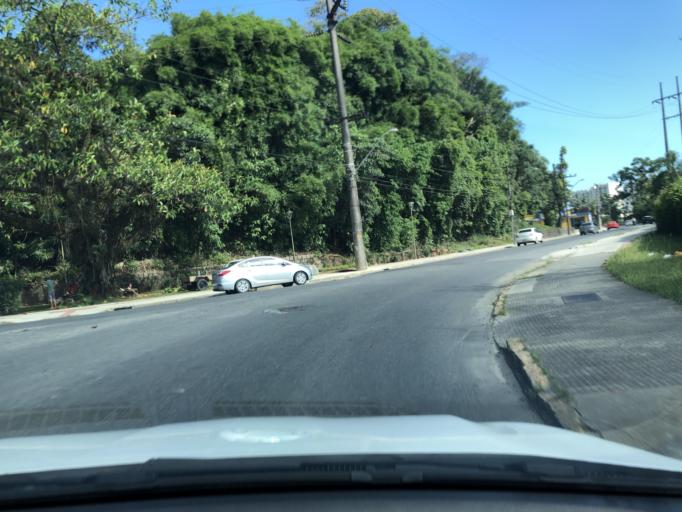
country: BR
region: Santa Catarina
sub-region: Joinville
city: Joinville
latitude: -26.3070
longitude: -48.8360
